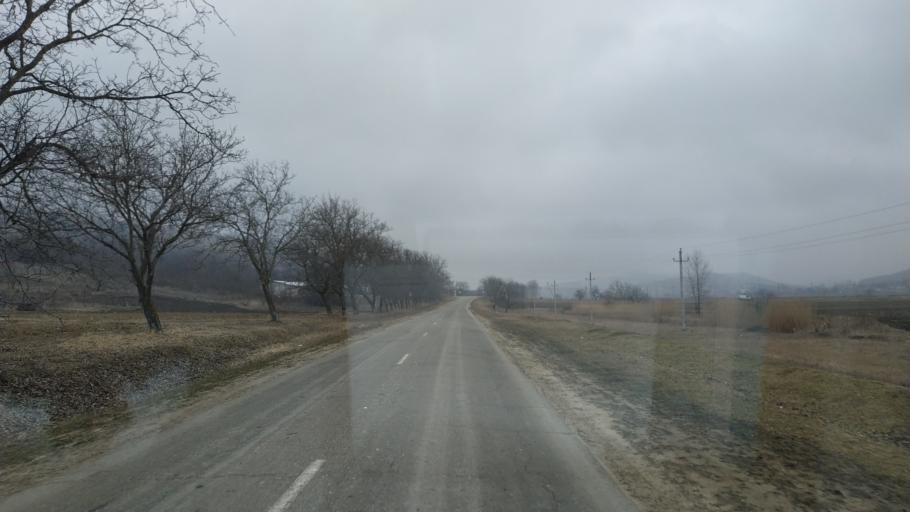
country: MD
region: Hincesti
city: Hincesti
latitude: 46.9659
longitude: 28.4803
